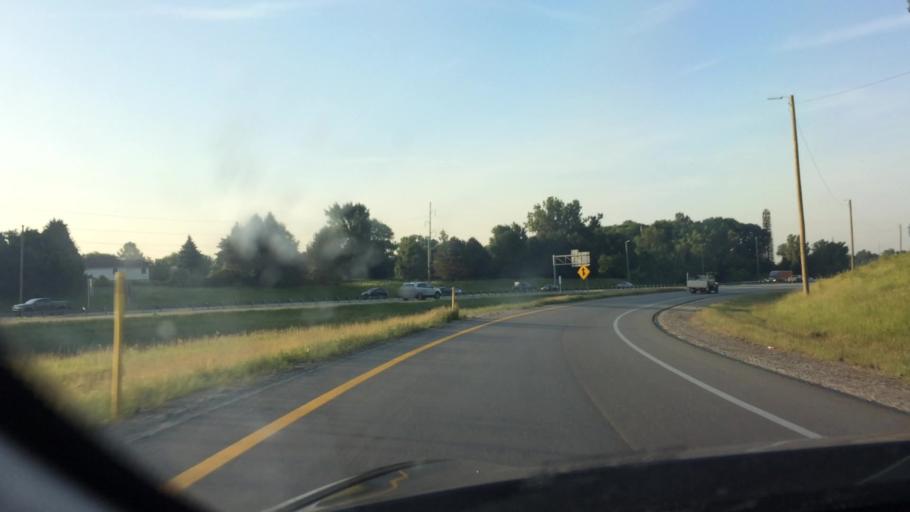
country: US
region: Ohio
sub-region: Lucas County
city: Holland
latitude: 41.6105
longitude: -83.6922
